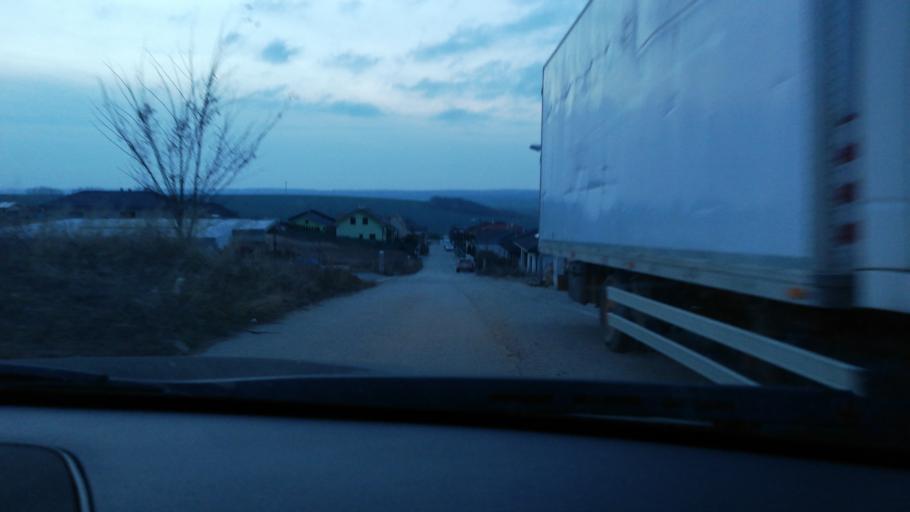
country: SK
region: Nitriansky
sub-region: Okres Nitra
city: Nitra
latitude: 48.3057
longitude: 17.9942
